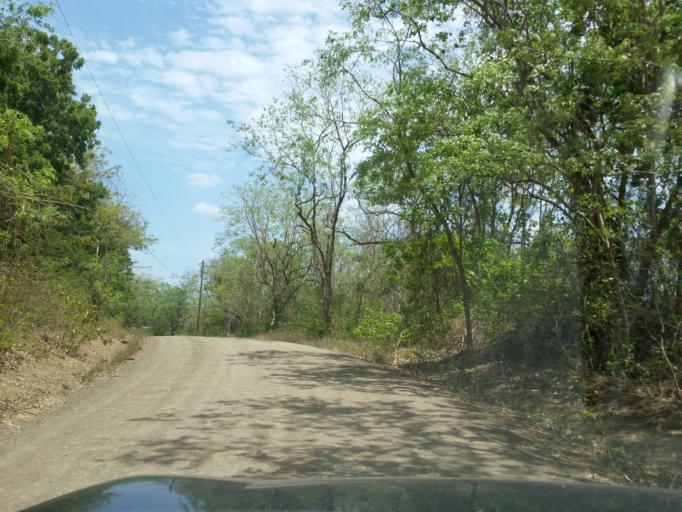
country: NI
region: Rivas
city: Tola
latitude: 11.5258
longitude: -86.0647
